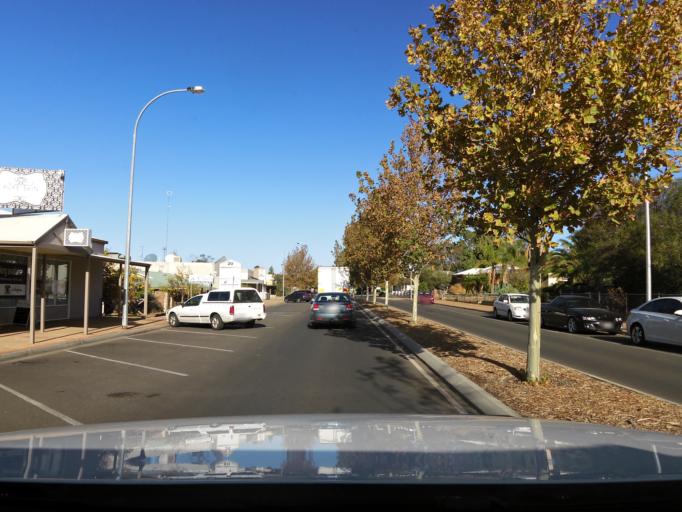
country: AU
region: South Australia
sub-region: Berri and Barmera
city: Berri
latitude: -34.2831
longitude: 140.6049
